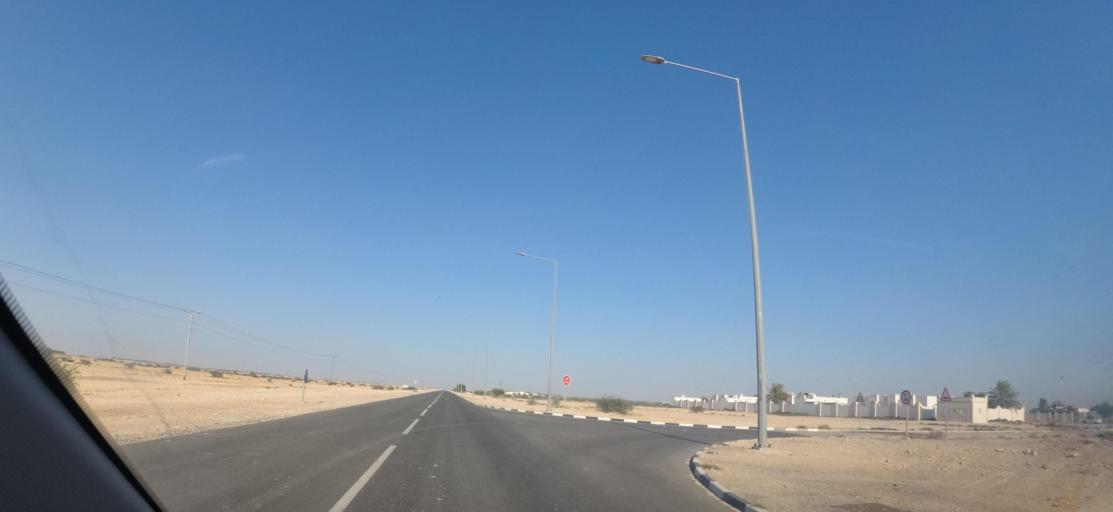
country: QA
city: Al Ghuwayriyah
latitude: 25.8373
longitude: 51.2574
